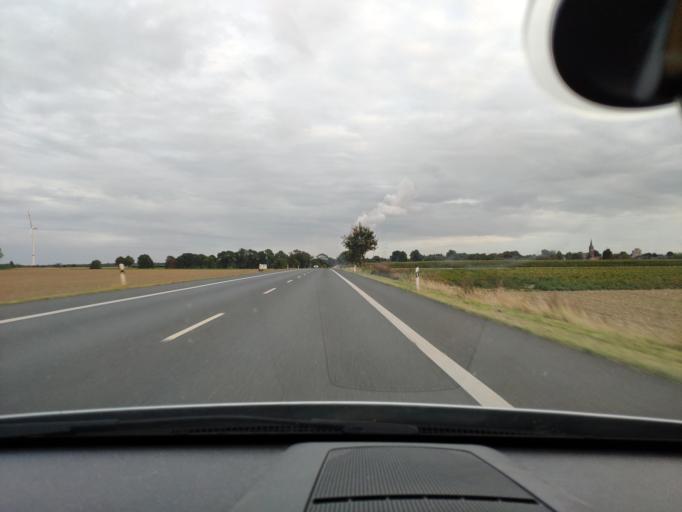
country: DE
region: North Rhine-Westphalia
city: Siersdorf
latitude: 50.9138
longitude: 6.2538
